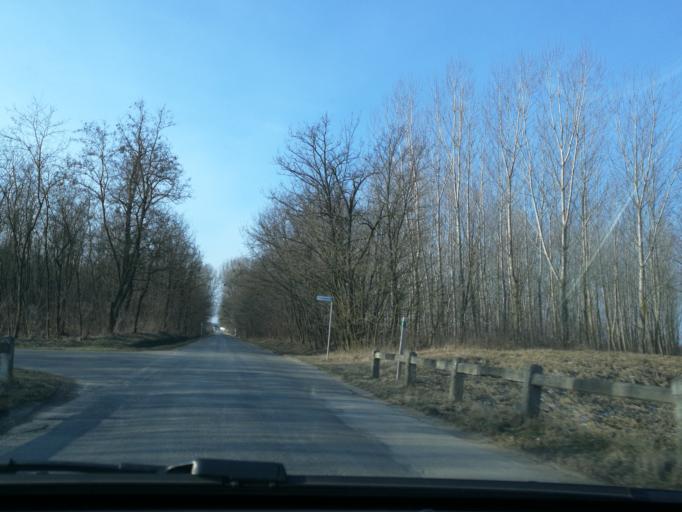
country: HU
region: Szabolcs-Szatmar-Bereg
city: Levelek
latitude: 48.0292
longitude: 21.9676
